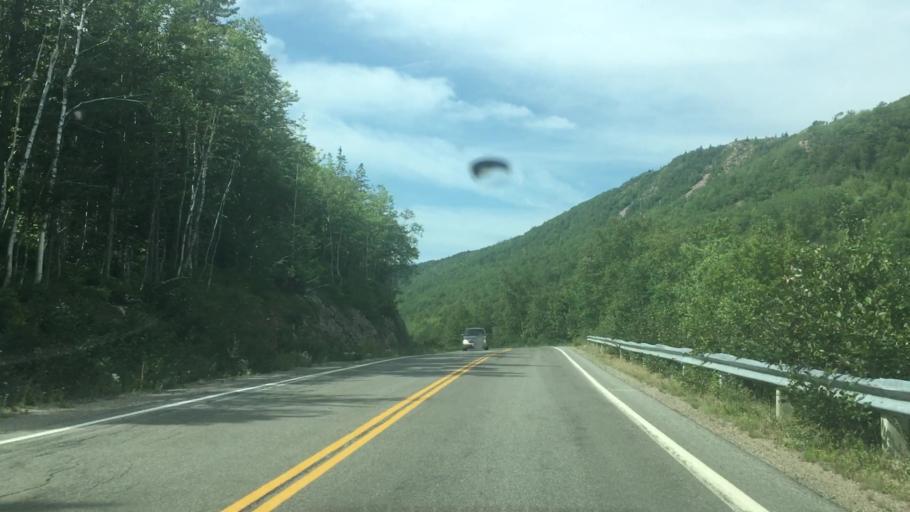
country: CA
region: Nova Scotia
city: Sydney Mines
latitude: 46.5815
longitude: -60.3922
